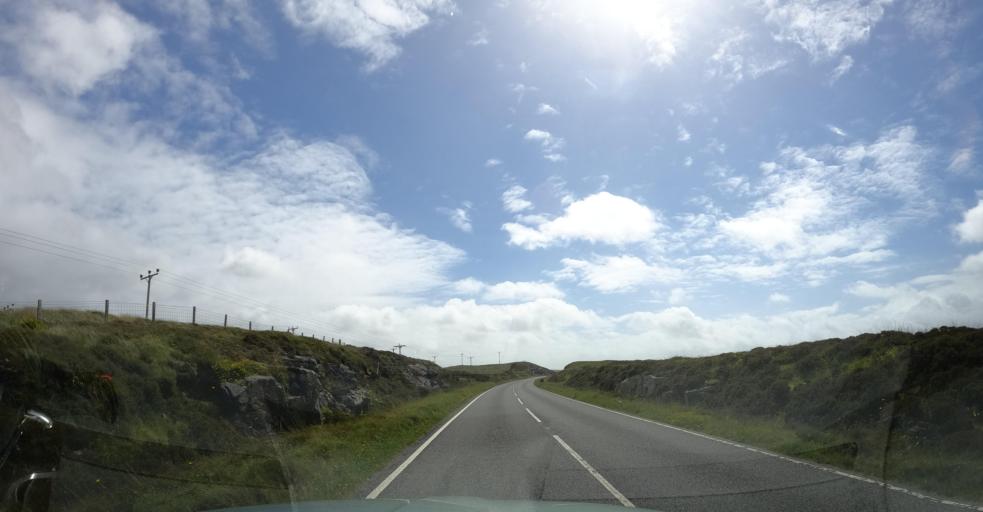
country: GB
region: Scotland
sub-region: Eilean Siar
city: Isle of South Uist
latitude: 57.2645
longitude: -7.3688
